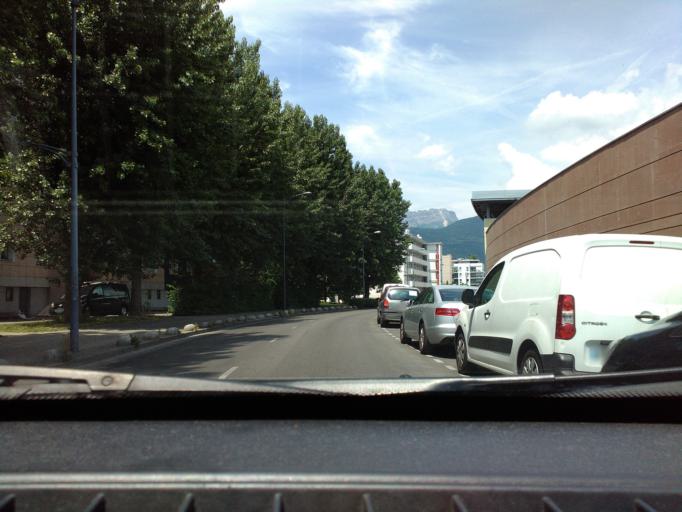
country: FR
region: Rhone-Alpes
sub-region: Departement de l'Isere
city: Saint-Martin-d'Heres
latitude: 45.1765
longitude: 5.7435
